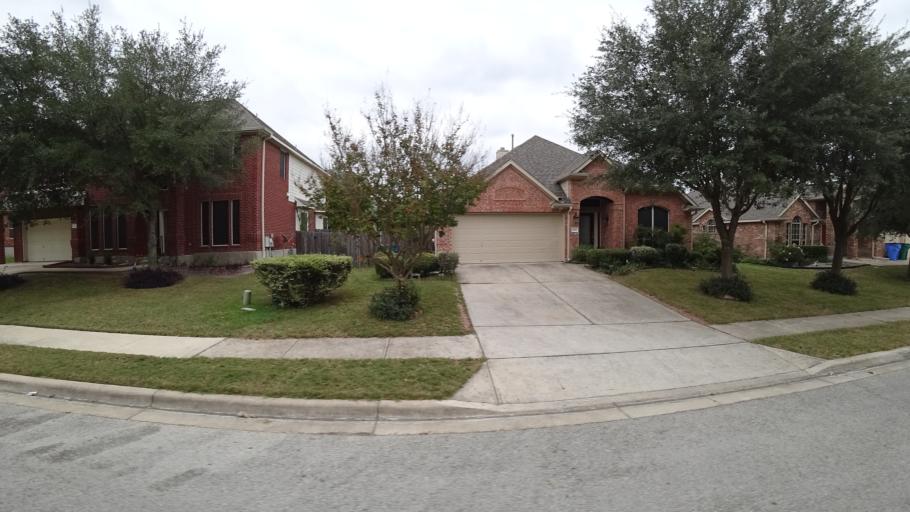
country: US
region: Texas
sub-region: Travis County
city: Pflugerville
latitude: 30.4524
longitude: -97.6243
